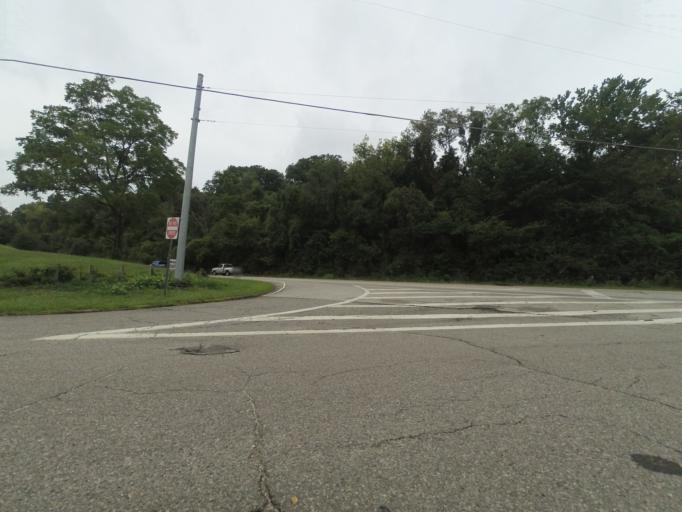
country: US
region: West Virginia
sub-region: Cabell County
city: Huntington
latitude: 38.4426
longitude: -82.4058
